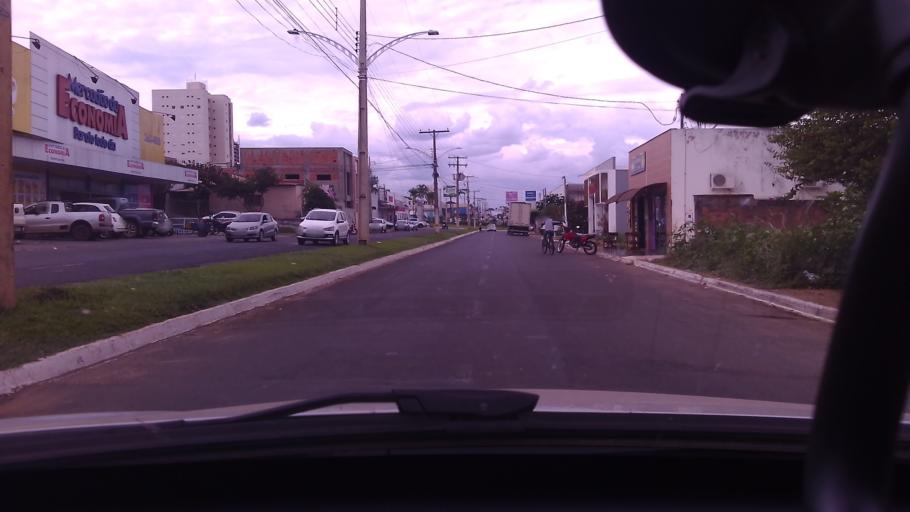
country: BR
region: Goias
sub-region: Mineiros
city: Mineiros
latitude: -17.5669
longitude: -52.5658
